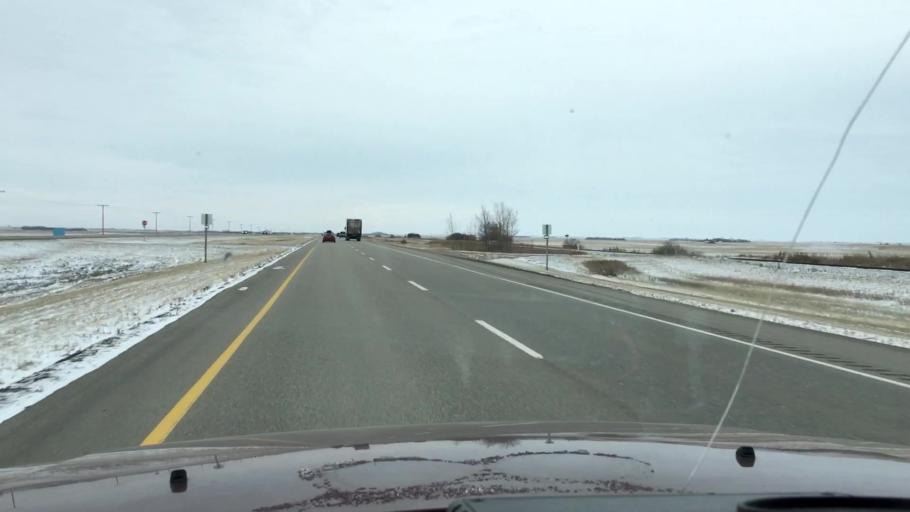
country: CA
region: Saskatchewan
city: Watrous
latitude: 51.1917
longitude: -105.9495
